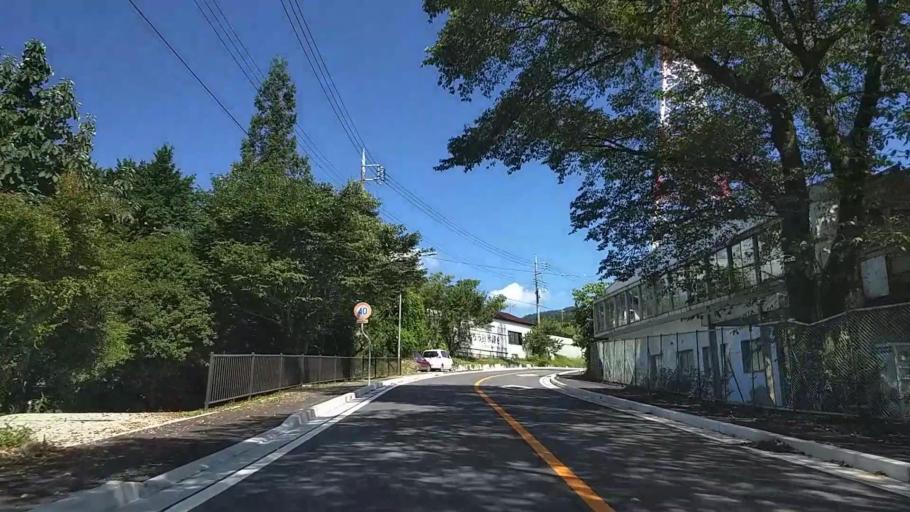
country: JP
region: Gunma
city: Annaka
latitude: 36.3386
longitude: 138.7269
